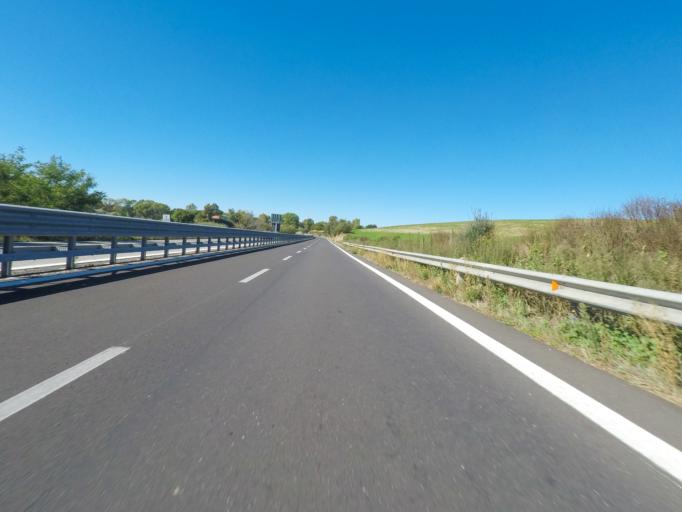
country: IT
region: Latium
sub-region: Provincia di Viterbo
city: Montalto di Castro
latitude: 42.3185
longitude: 11.6516
